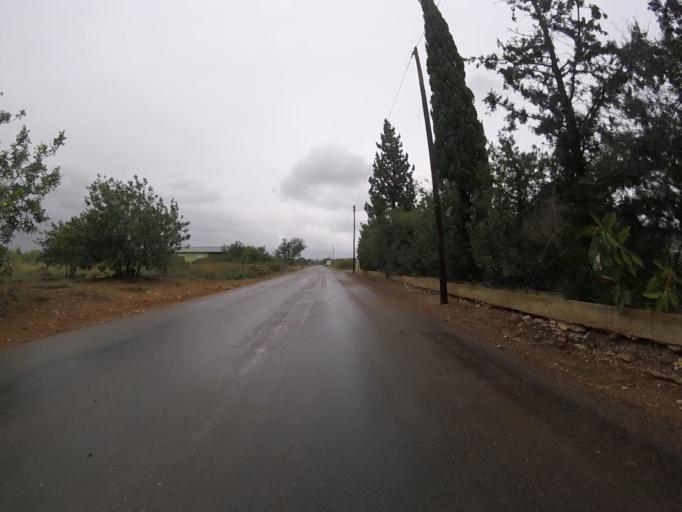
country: ES
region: Valencia
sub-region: Provincia de Castello
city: Alcoceber
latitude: 40.2437
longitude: 0.2483
